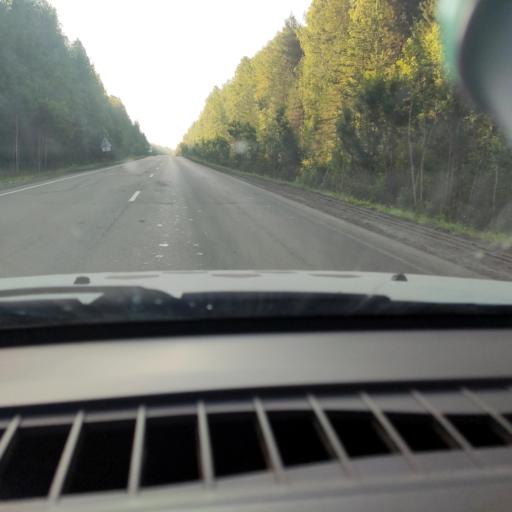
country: RU
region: Kirov
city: Chernaya Kholunitsa
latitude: 58.8696
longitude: 51.5481
